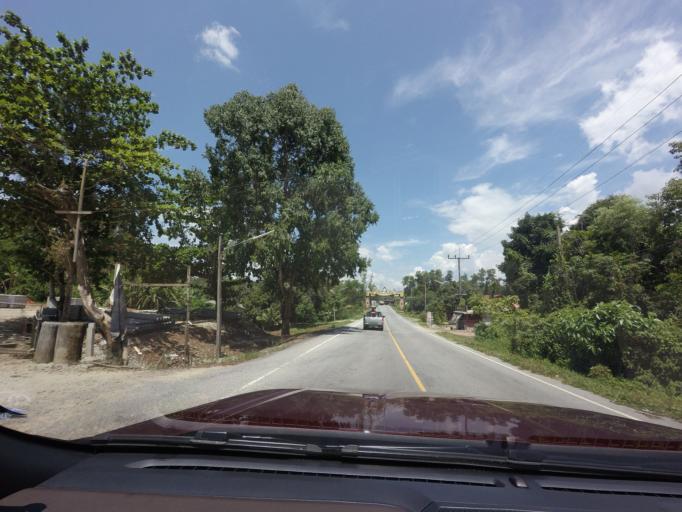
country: TH
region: Narathiwat
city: Chanae
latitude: 6.1448
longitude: 101.7026
